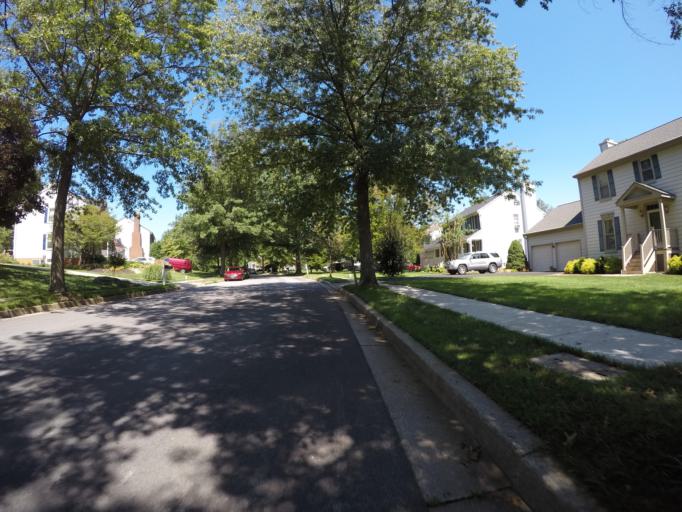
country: US
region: Maryland
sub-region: Howard County
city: Columbia
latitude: 39.2884
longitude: -76.8734
